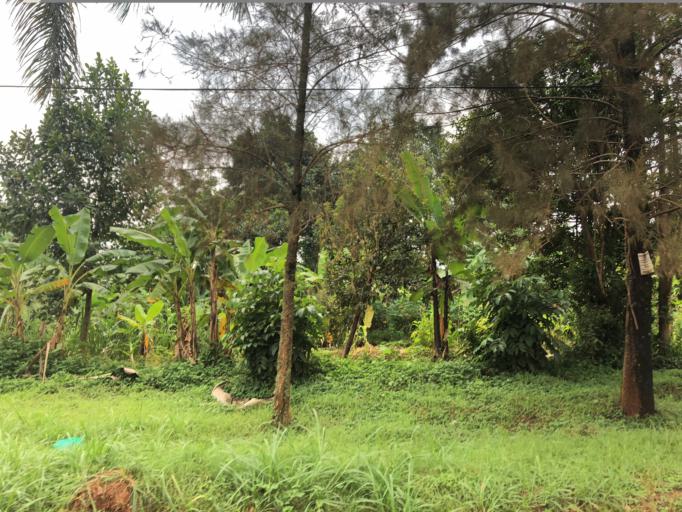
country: UG
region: Central Region
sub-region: Mukono District
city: Mukono
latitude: 0.3609
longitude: 32.7438
